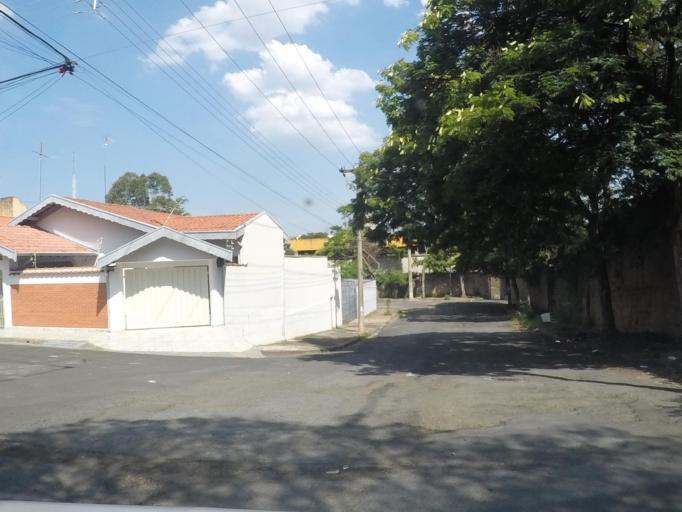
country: BR
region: Sao Paulo
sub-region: Sumare
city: Sumare
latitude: -22.8170
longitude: -47.2595
